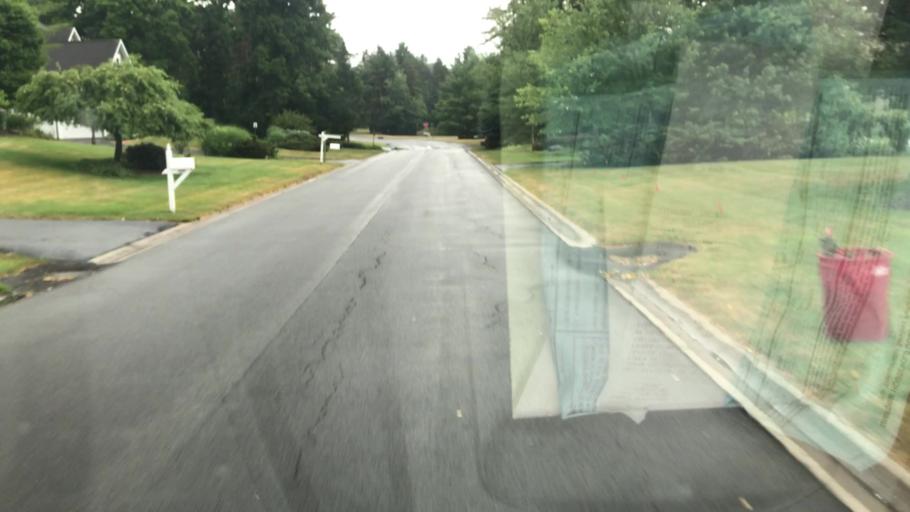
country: US
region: New York
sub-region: Onondaga County
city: Manlius
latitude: 42.9877
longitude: -75.9789
